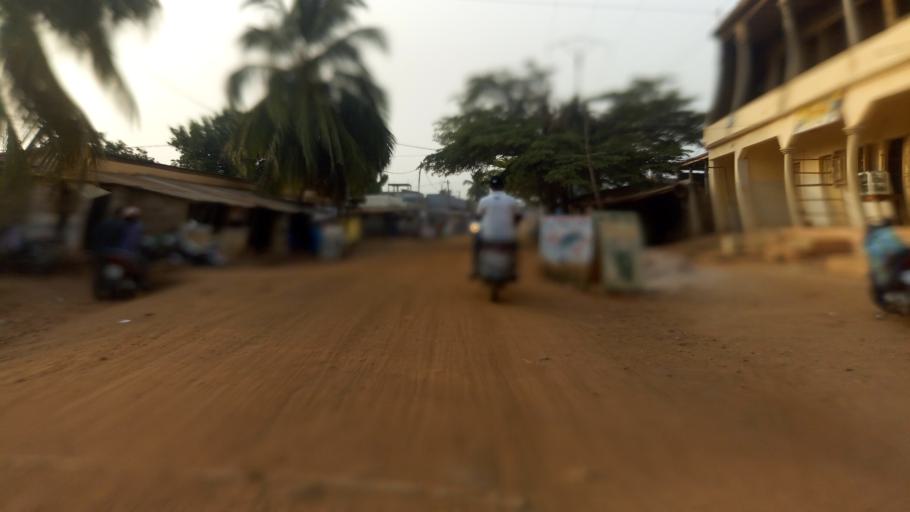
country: TG
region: Maritime
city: Tsevie
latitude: 6.3178
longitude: 1.2196
